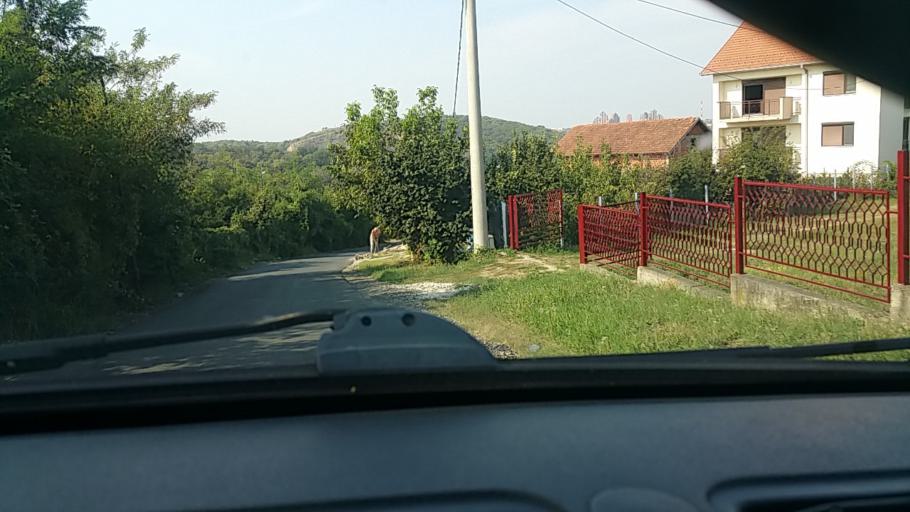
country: RS
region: Central Serbia
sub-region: Belgrade
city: Rakovica
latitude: 44.7354
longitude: 20.4565
